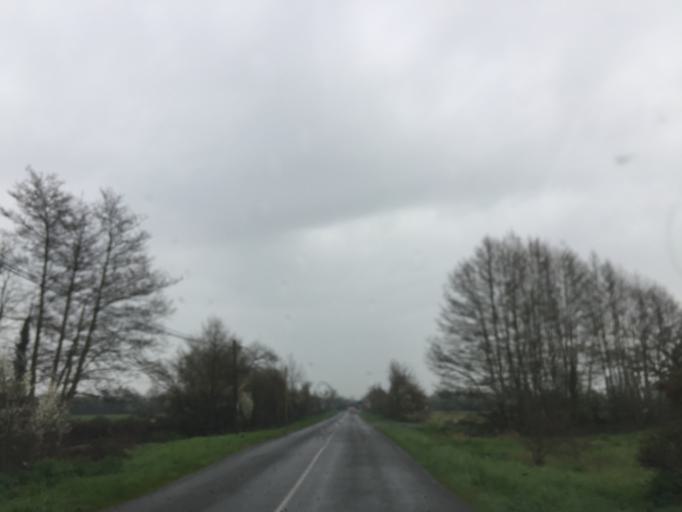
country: FR
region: Pays de la Loire
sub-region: Departement de la Loire-Atlantique
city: Casson
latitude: 47.3993
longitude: -1.5281
